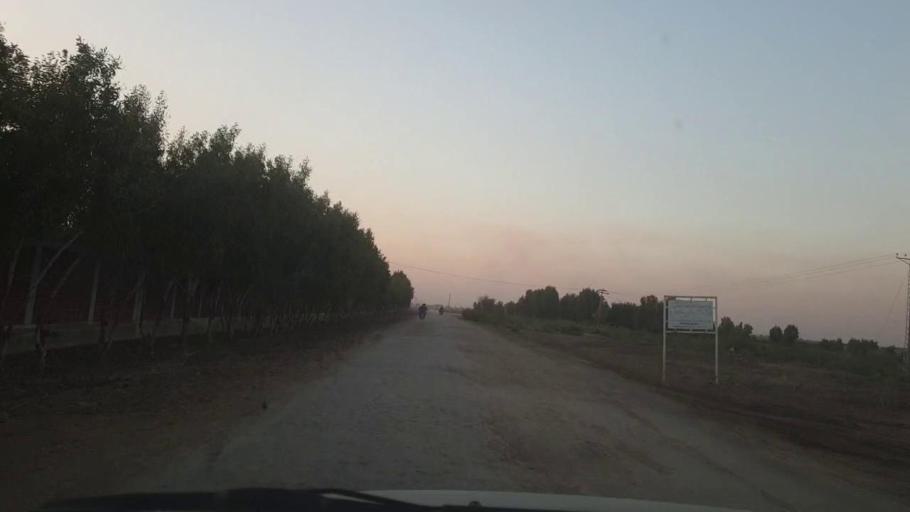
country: PK
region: Sindh
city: Mirpur Khas
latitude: 25.4869
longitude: 69.0423
